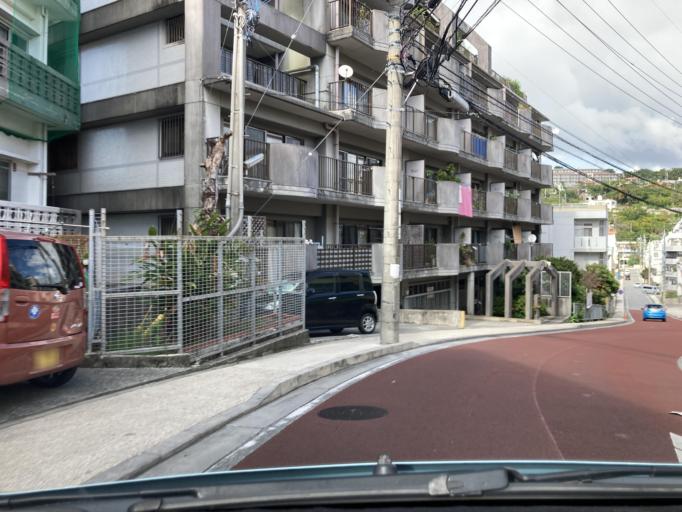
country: JP
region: Okinawa
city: Naha-shi
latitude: 26.2142
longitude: 127.7089
